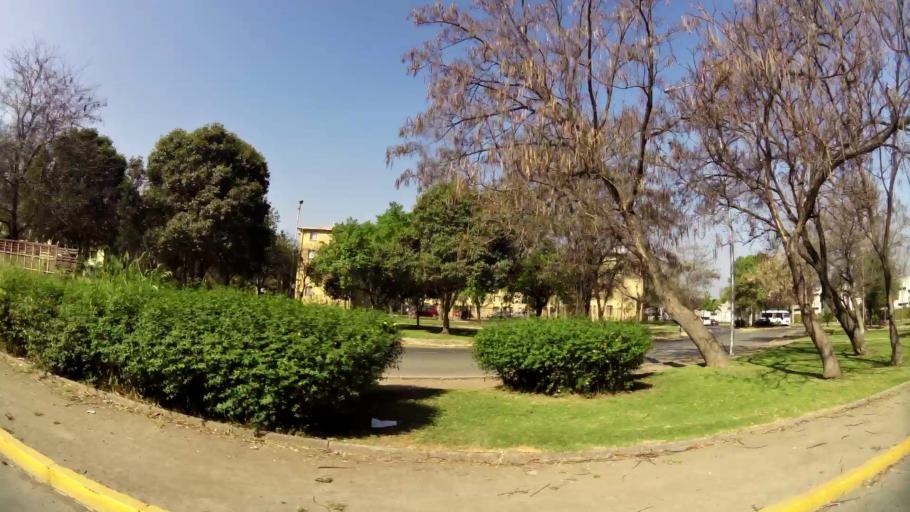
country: CL
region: Santiago Metropolitan
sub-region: Provincia de Santiago
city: Santiago
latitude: -33.4706
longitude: -70.6230
